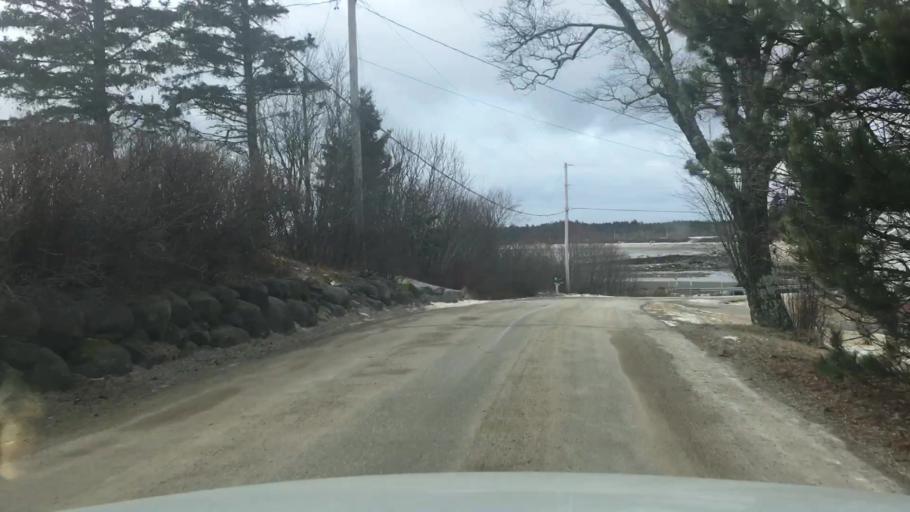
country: US
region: Maine
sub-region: Washington County
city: Machias
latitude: 44.6088
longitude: -67.4756
